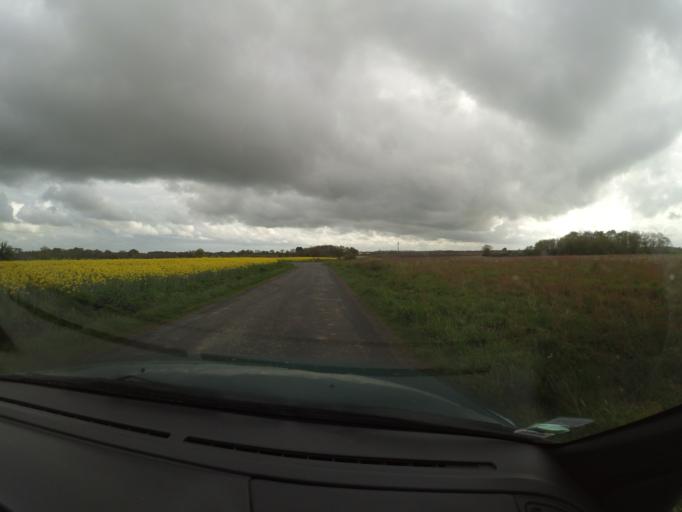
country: FR
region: Pays de la Loire
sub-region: Departement de la Loire-Atlantique
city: Maisdon-sur-Sevre
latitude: 47.0854
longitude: -1.3721
